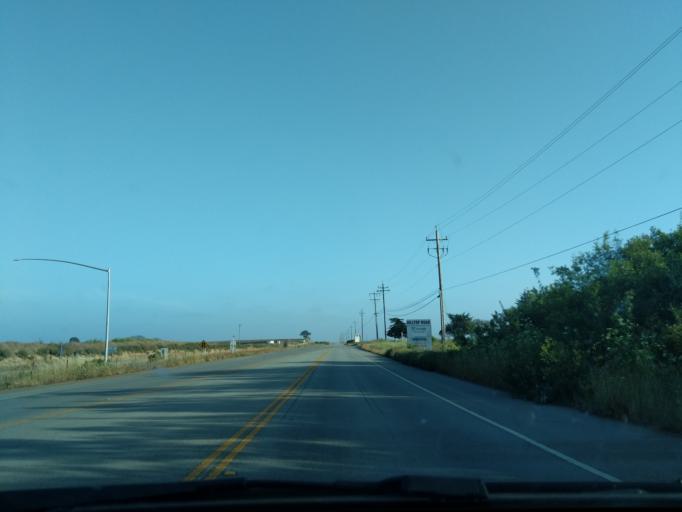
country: US
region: California
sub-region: Monterey County
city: Las Lomas
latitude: 36.8667
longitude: -121.7714
